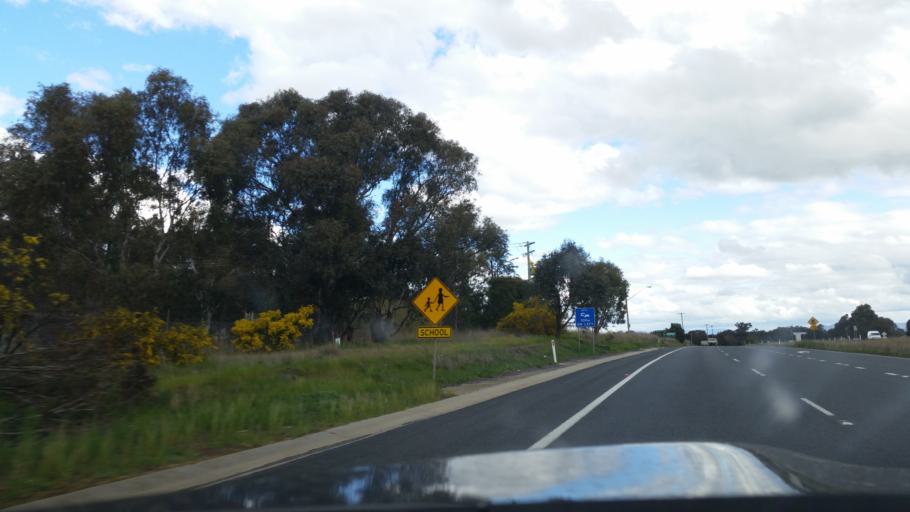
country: AU
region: New South Wales
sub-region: Albury Municipality
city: Lavington
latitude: -35.9690
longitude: 147.0048
